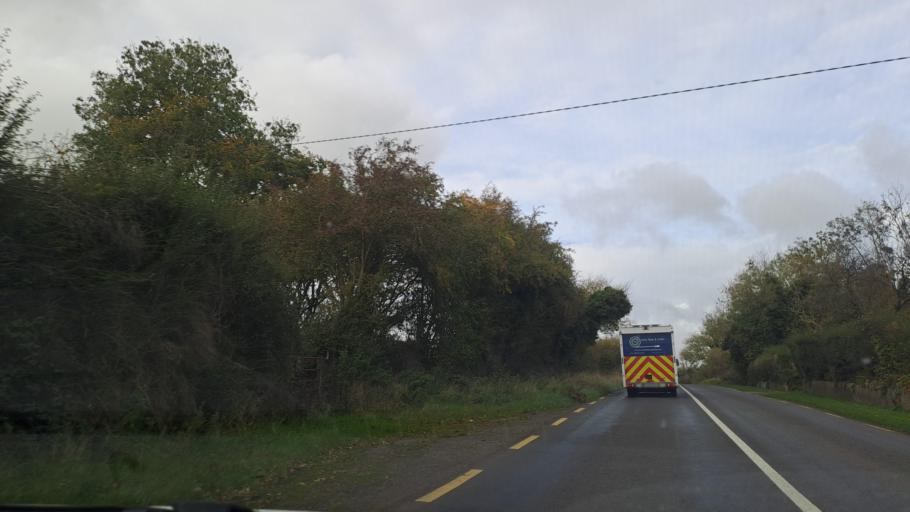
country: IE
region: Ulster
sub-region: An Cabhan
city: Kingscourt
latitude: 53.8048
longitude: -6.7365
